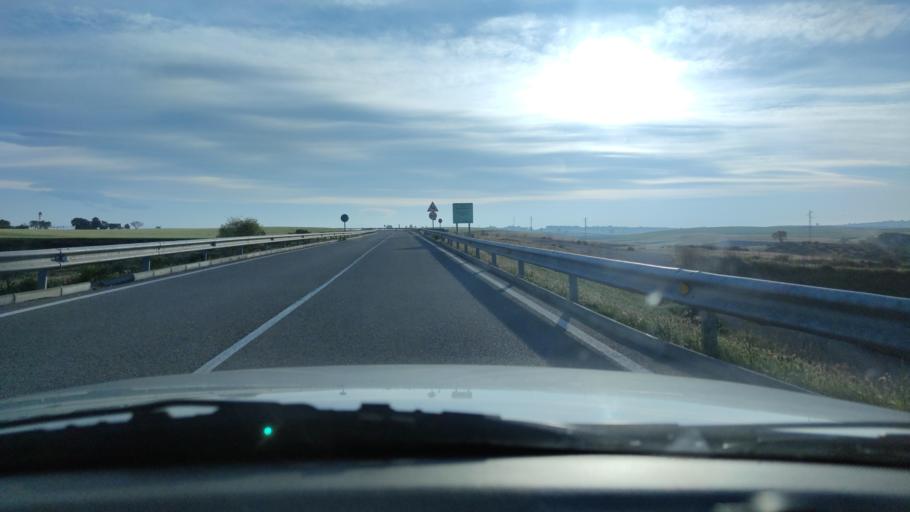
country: ES
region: Catalonia
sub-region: Provincia de Lleida
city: Castellsera
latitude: 41.7677
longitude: 1.0040
